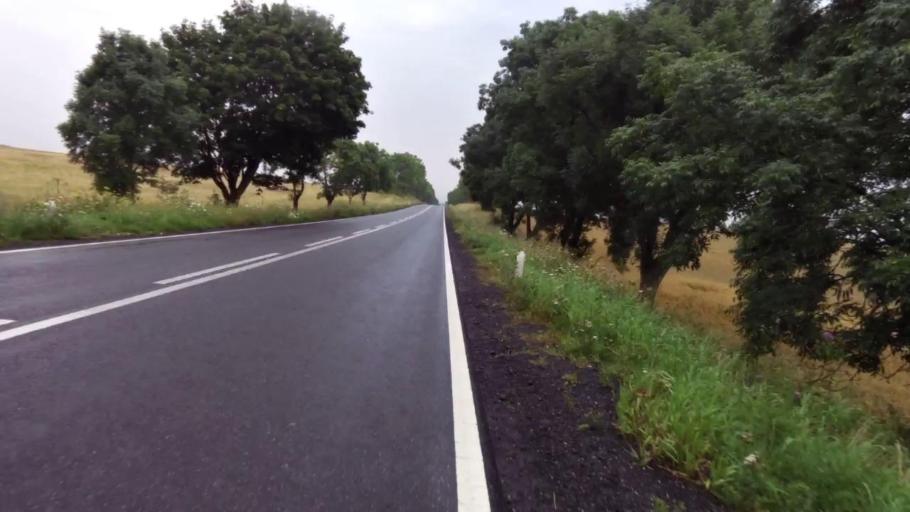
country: PL
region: West Pomeranian Voivodeship
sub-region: Powiat stargardzki
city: Insko
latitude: 53.4528
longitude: 15.5764
